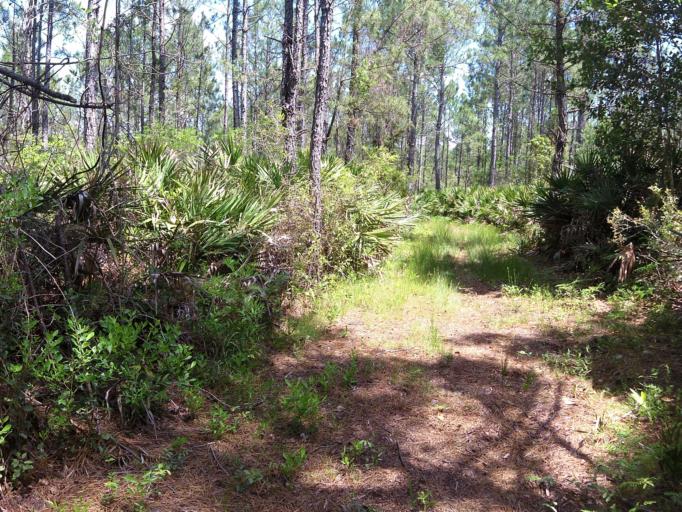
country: US
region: Florida
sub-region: Nassau County
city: Yulee
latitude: 30.4966
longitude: -81.4960
